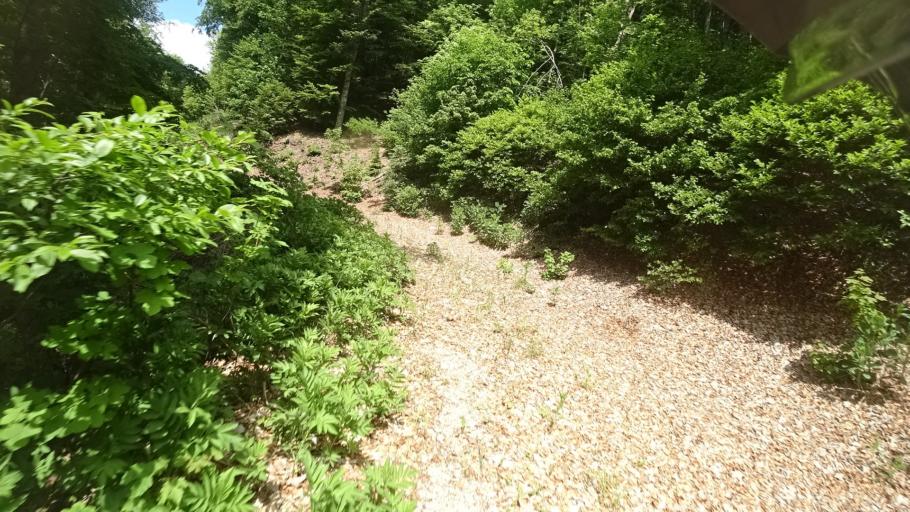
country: BA
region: Federation of Bosnia and Herzegovina
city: Orasac
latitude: 44.5658
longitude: 15.8662
